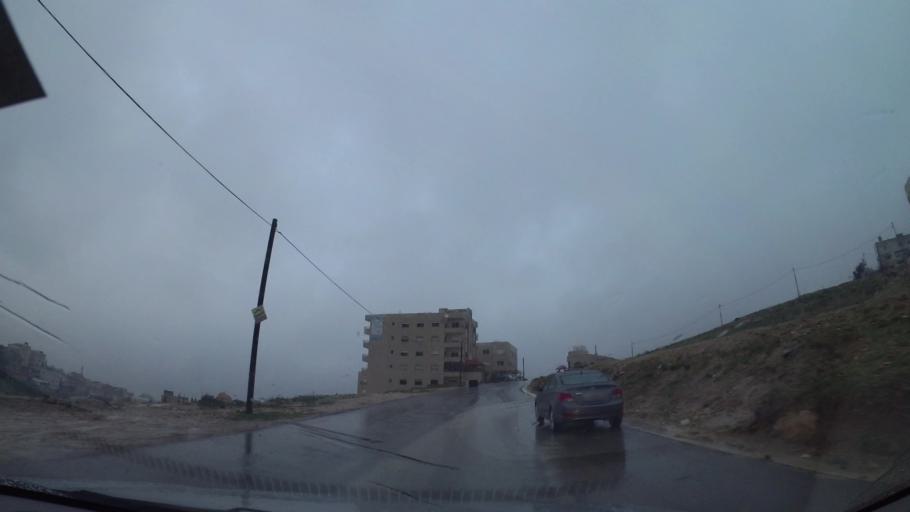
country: JO
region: Amman
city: Al Jubayhah
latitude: 32.0267
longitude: 35.8423
